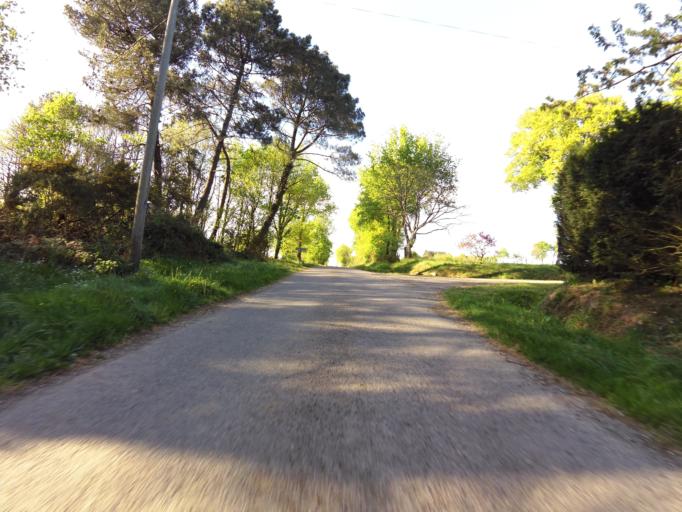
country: FR
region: Brittany
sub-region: Departement du Morbihan
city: Molac
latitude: 47.7365
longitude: -2.4759
